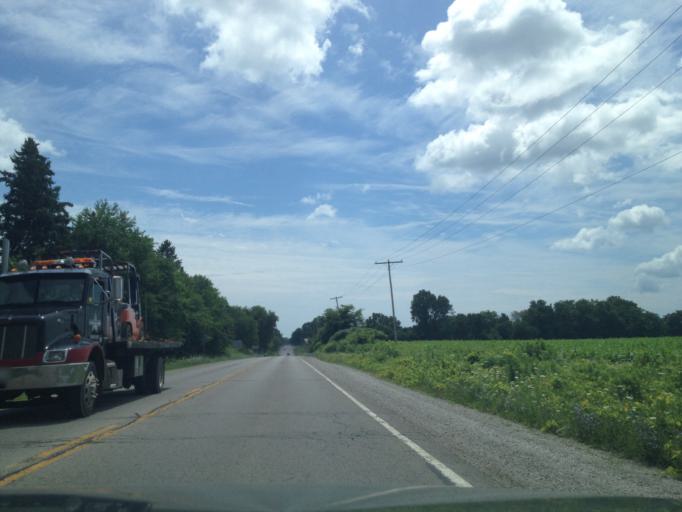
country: CA
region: Ontario
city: Norfolk County
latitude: 42.7824
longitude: -80.2839
